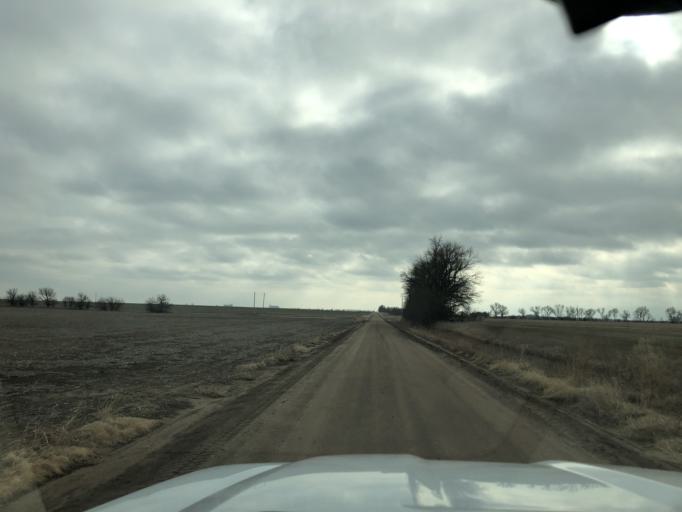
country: US
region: Kansas
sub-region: Reno County
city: Nickerson
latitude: 38.0164
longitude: -98.2158
